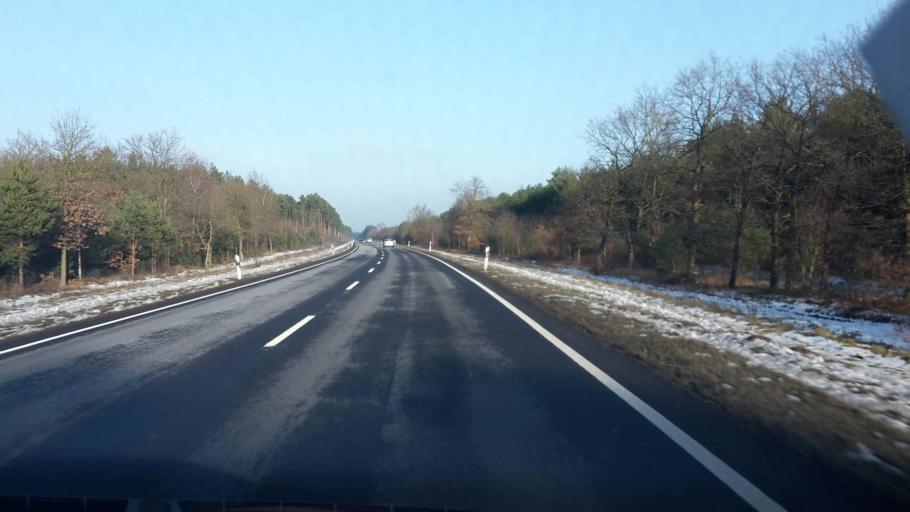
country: DE
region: Brandenburg
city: Weisen
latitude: 53.0371
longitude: 11.8066
